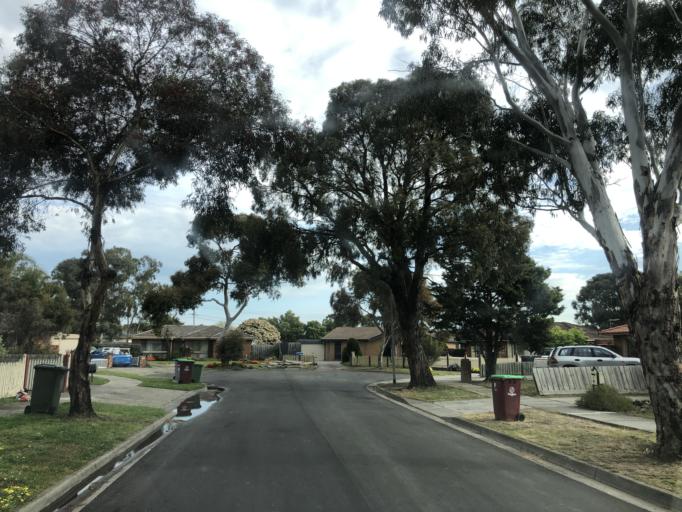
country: AU
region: Victoria
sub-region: Casey
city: Hampton Park
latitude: -38.0251
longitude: 145.2511
